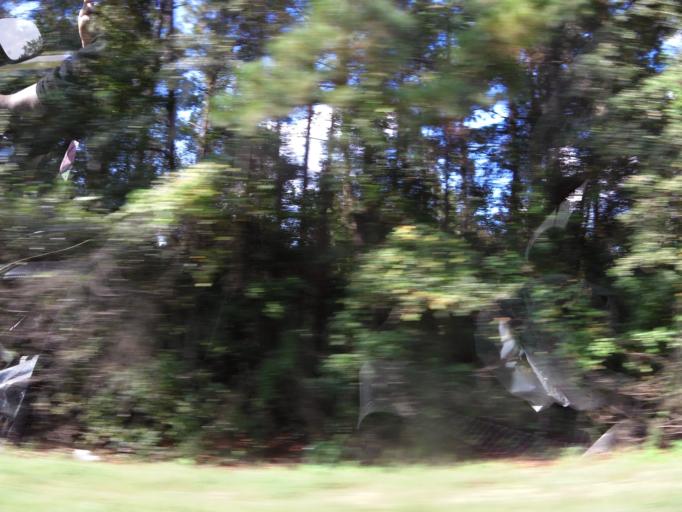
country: US
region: Georgia
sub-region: Brooks County
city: Quitman
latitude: 30.7852
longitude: -83.6165
